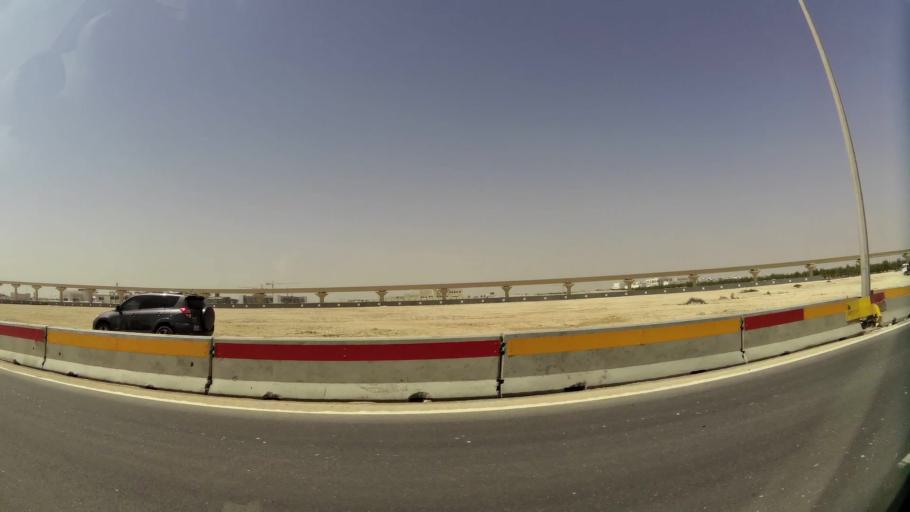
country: QA
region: Baladiyat Umm Salal
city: Umm Salal Muhammad
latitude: 25.3873
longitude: 51.4924
